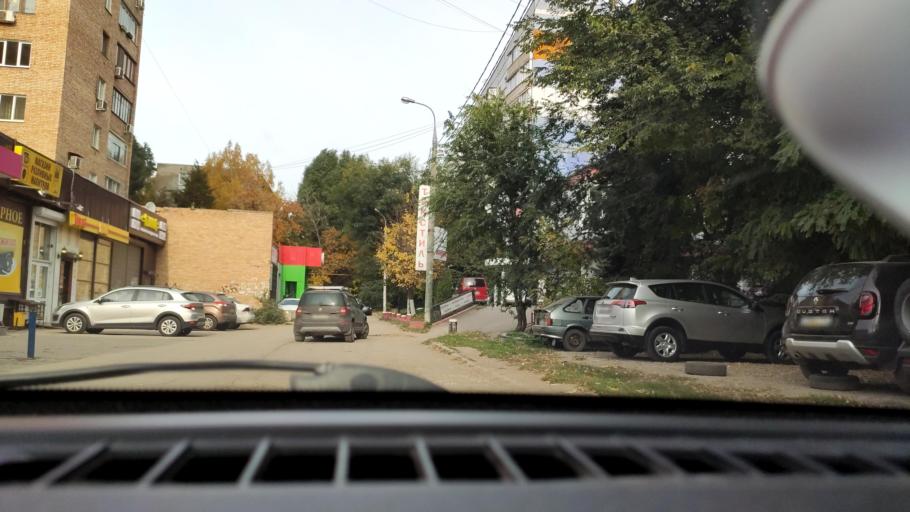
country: RU
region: Samara
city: Samara
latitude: 53.2318
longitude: 50.2596
